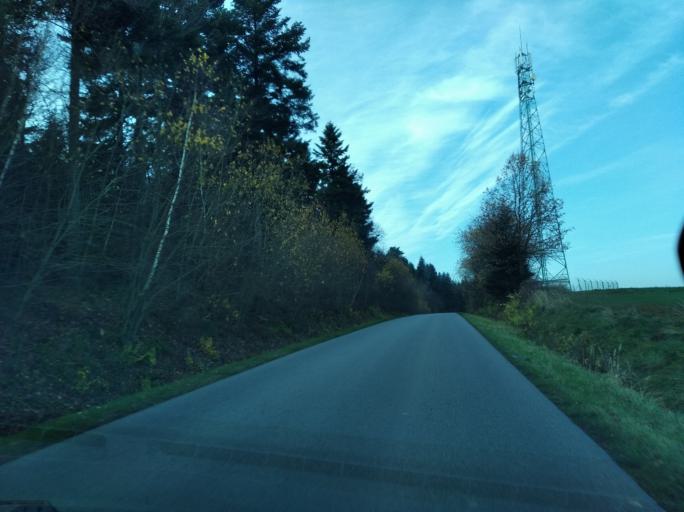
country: PL
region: Subcarpathian Voivodeship
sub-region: Powiat ropczycko-sedziszowski
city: Zagorzyce
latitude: 49.9552
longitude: 21.6945
